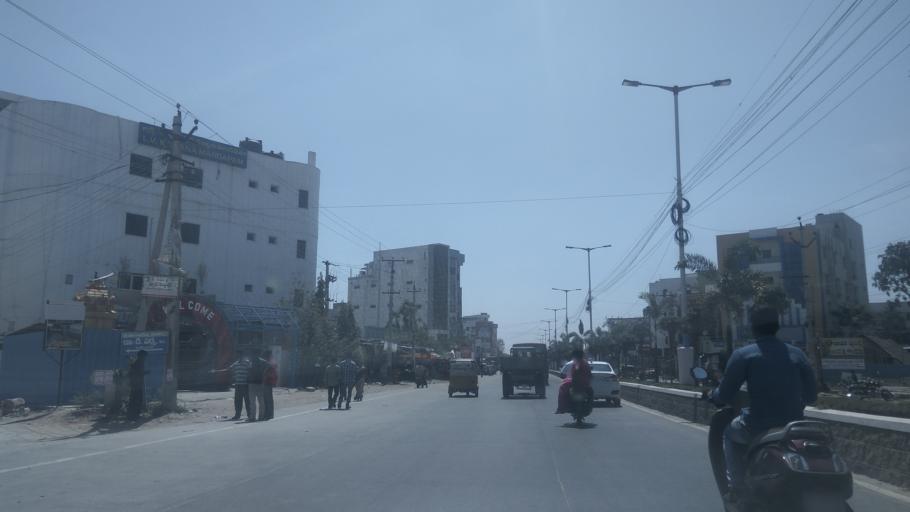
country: IN
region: Andhra Pradesh
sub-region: Chittoor
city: Tirupati
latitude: 13.6160
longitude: 79.4353
